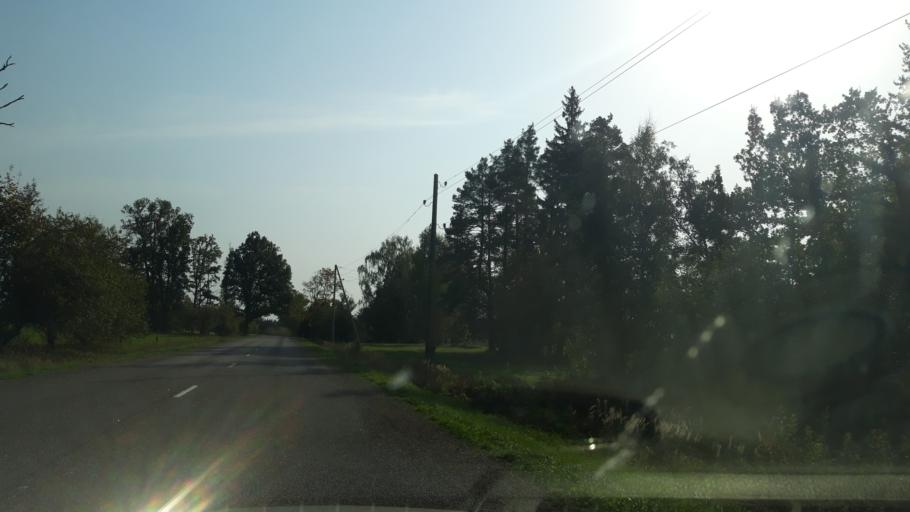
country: LV
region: Koceni
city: Koceni
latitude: 57.6277
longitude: 25.2665
